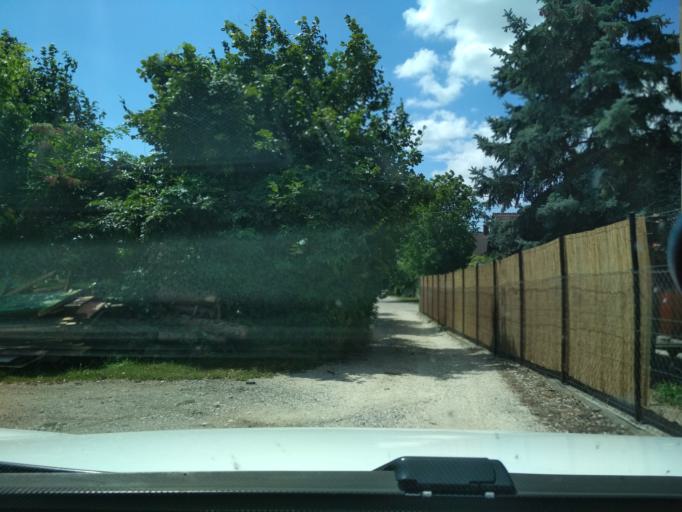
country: HU
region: Fejer
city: Velence
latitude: 47.2217
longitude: 18.6645
